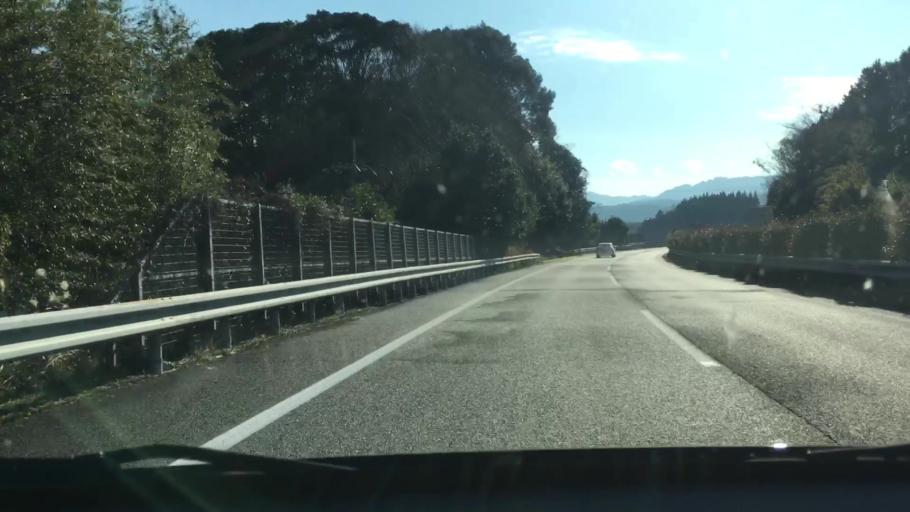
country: JP
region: Kumamoto
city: Hitoyoshi
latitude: 32.2168
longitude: 130.7796
